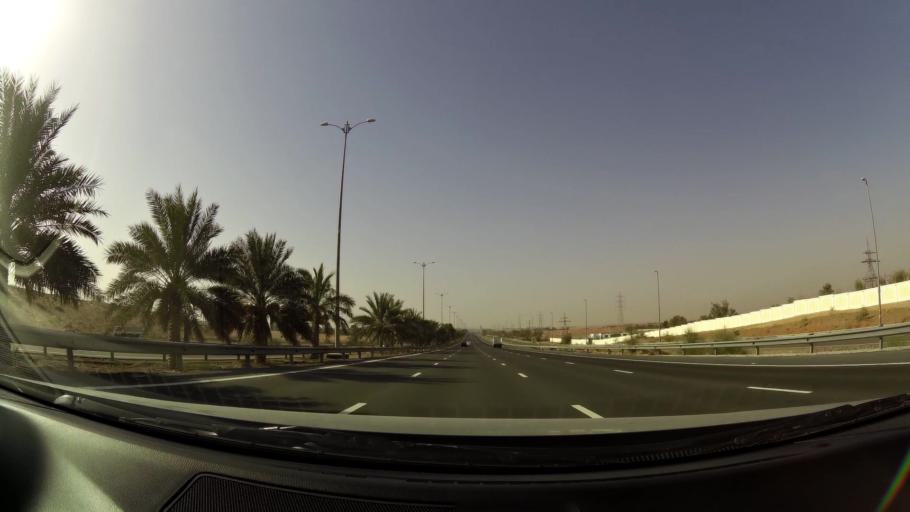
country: OM
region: Al Buraimi
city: Al Buraymi
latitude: 24.4849
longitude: 55.7732
